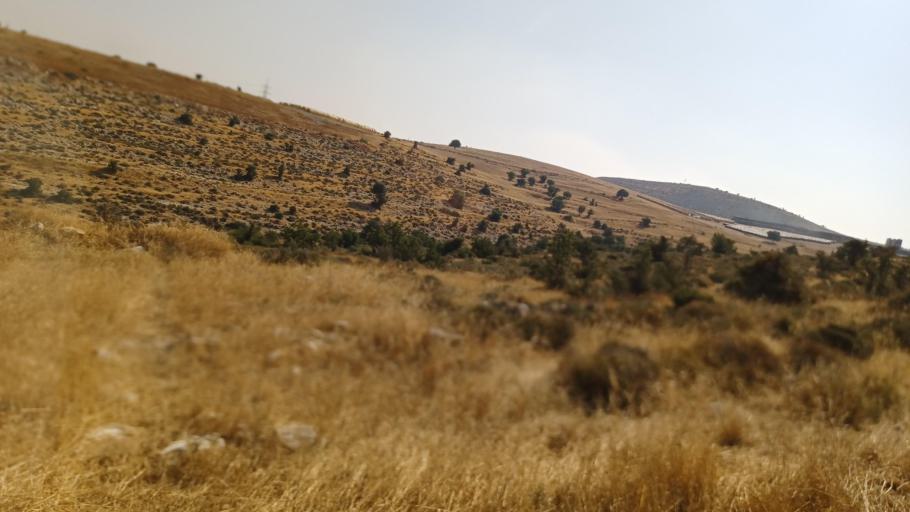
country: CY
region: Lefkosia
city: Lympia
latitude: 34.9817
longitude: 33.4810
